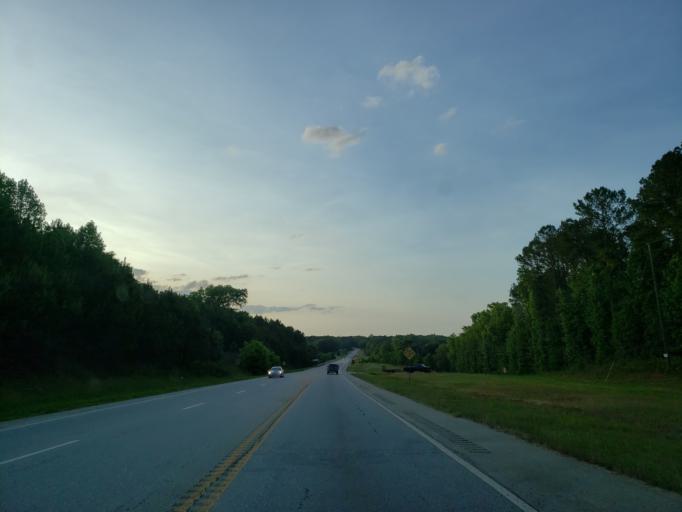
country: US
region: Georgia
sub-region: Coweta County
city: Newnan
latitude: 33.4731
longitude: -84.8992
